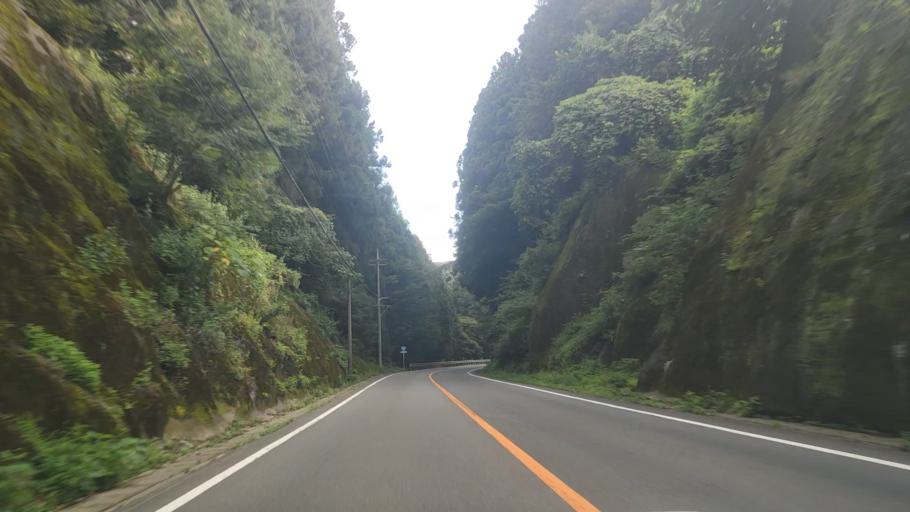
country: JP
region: Gunma
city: Omamacho-omama
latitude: 36.5067
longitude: 139.2954
